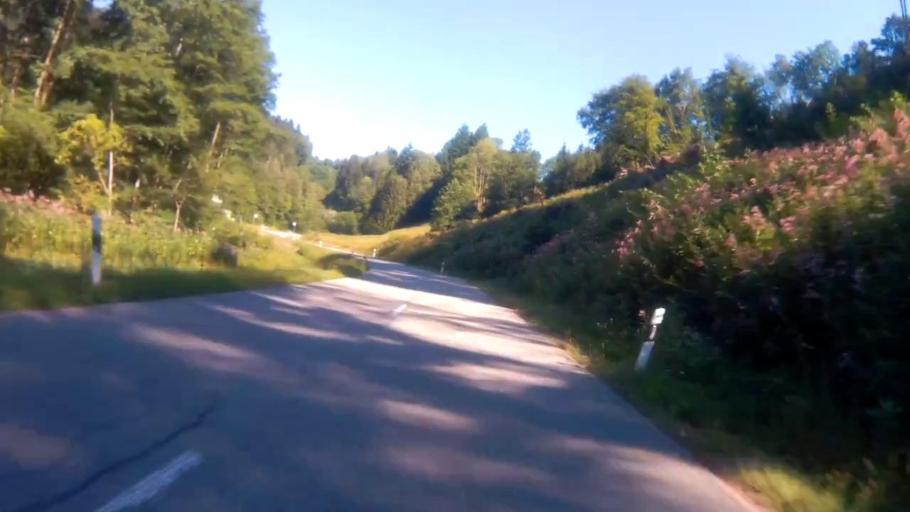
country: DE
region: Baden-Wuerttemberg
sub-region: Freiburg Region
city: Hausen
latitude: 47.7133
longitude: 7.7955
